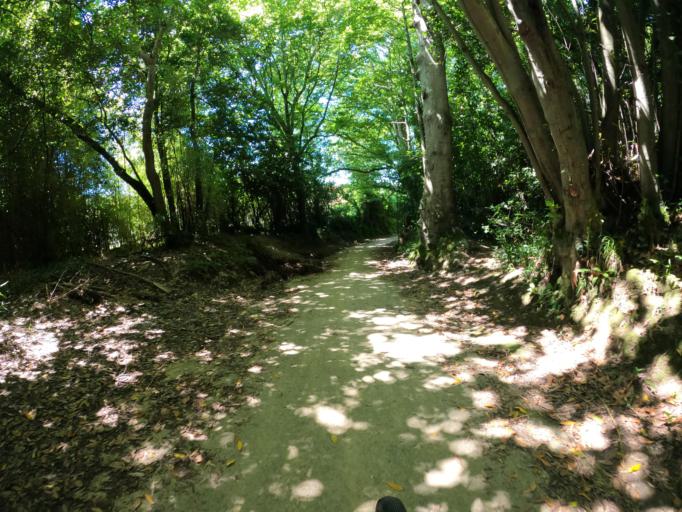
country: FR
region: Aquitaine
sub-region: Departement des Pyrenees-Atlantiques
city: Boucau
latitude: 43.5272
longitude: -1.4544
